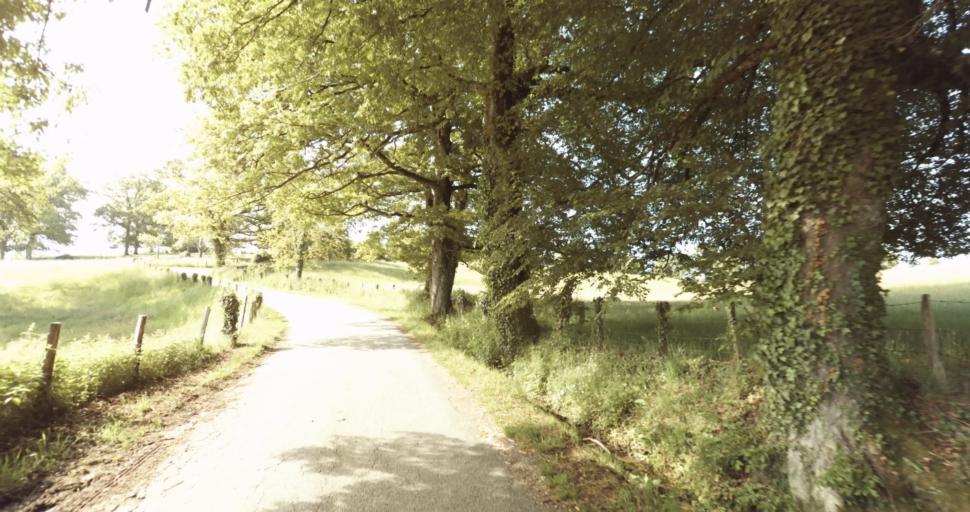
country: FR
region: Limousin
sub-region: Departement de la Haute-Vienne
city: Solignac
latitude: 45.7075
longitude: 1.2640
